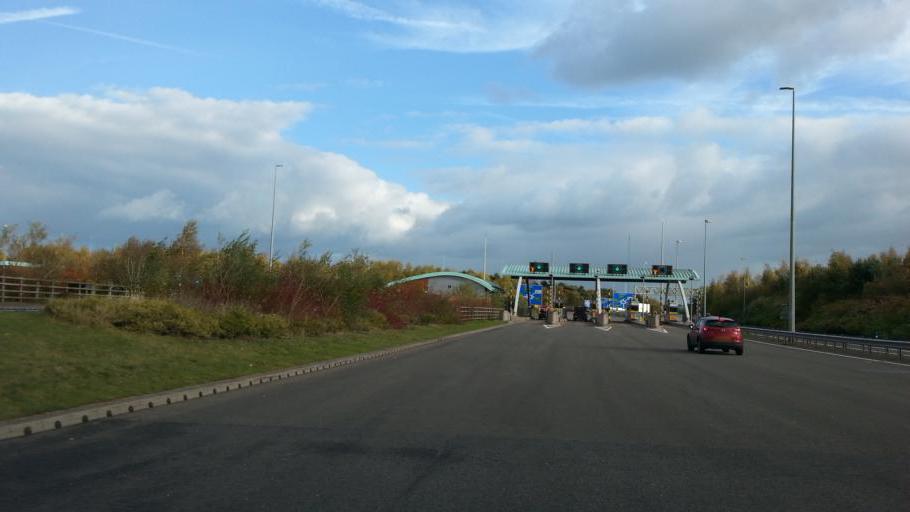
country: GB
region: England
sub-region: Staffordshire
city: Shenstone
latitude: 52.6394
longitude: -1.8091
